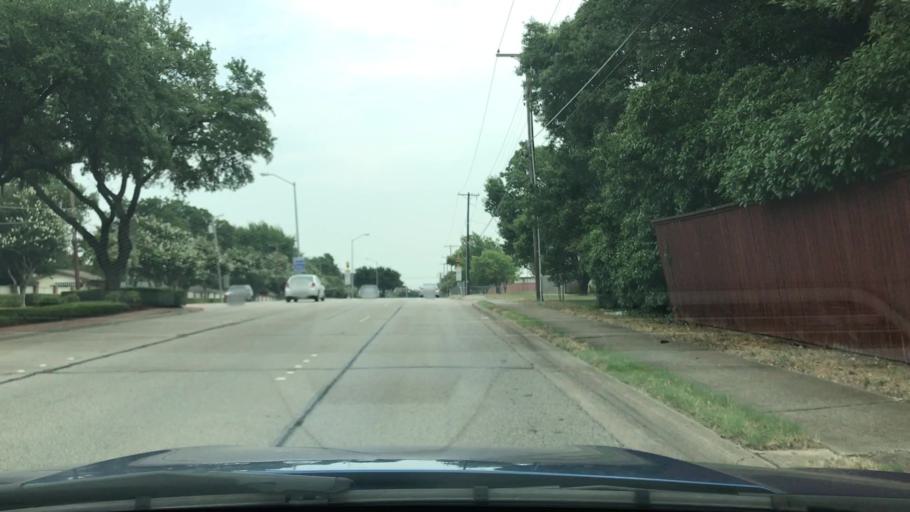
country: US
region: Texas
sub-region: Dallas County
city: Richardson
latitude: 32.9621
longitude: -96.7660
